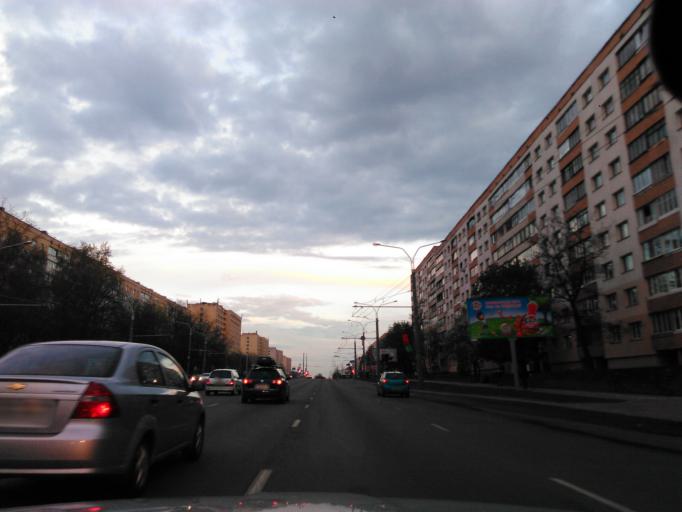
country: BY
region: Minsk
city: Novoye Medvezhino
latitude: 53.9053
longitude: 27.4960
